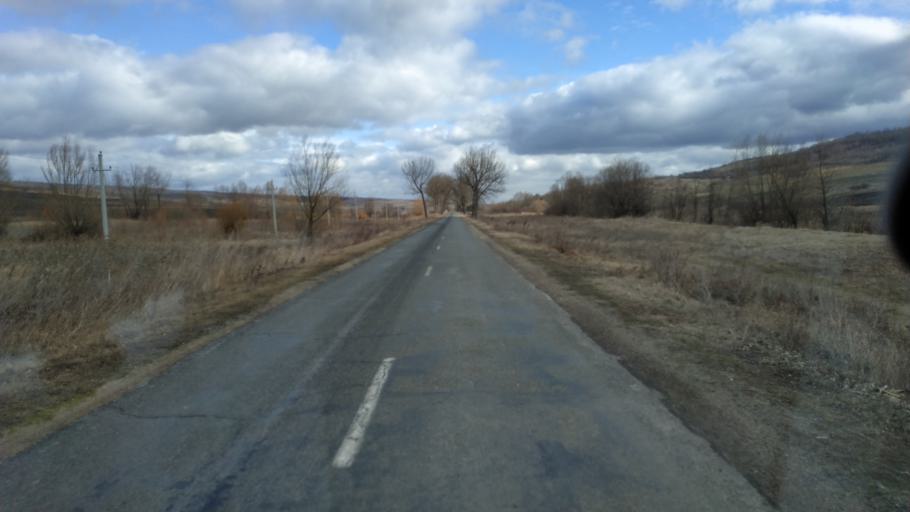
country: MD
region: Calarasi
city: Calarasi
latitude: 47.1384
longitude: 28.3305
